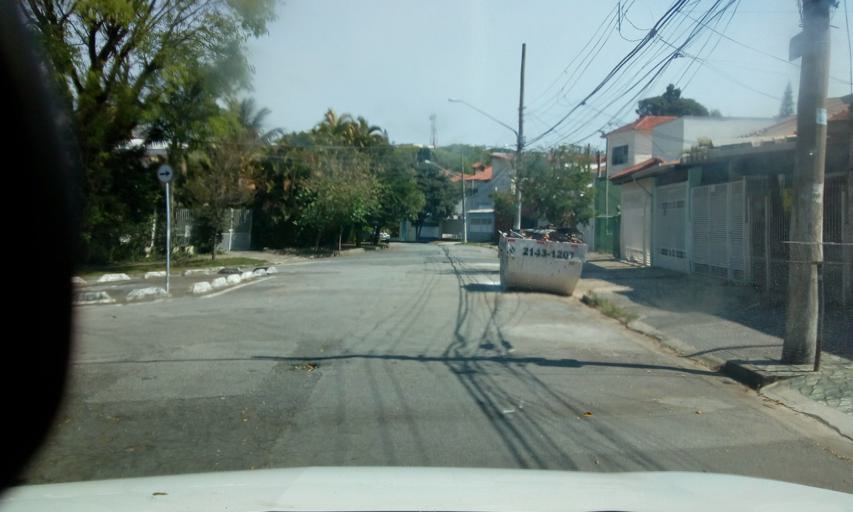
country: BR
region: Sao Paulo
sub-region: Osasco
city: Osasco
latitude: -23.5226
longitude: -46.7145
